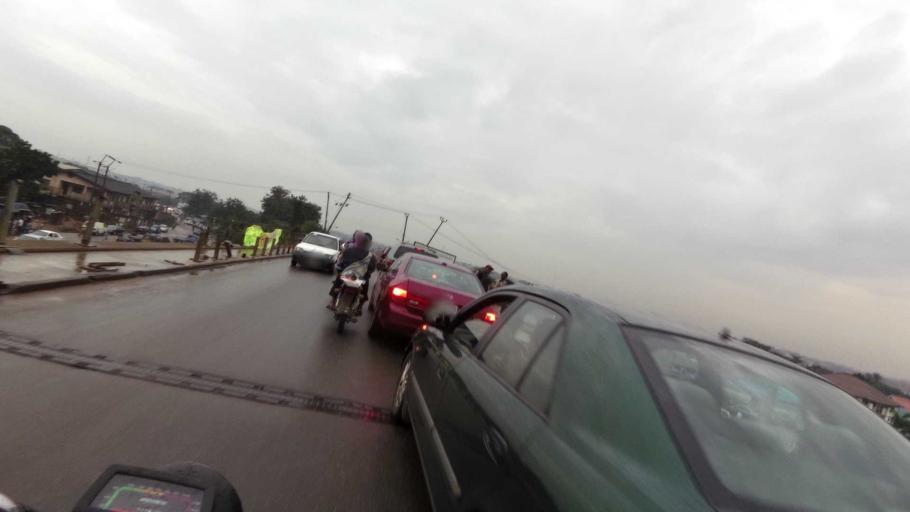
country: NG
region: Oyo
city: Ibadan
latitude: 7.4231
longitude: 3.9363
